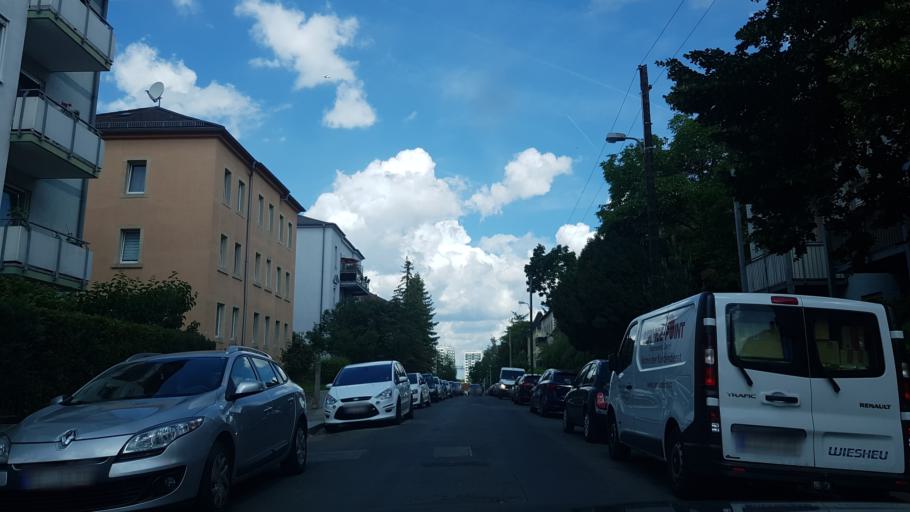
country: DE
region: Saxony
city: Freital
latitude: 51.0375
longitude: 13.6827
